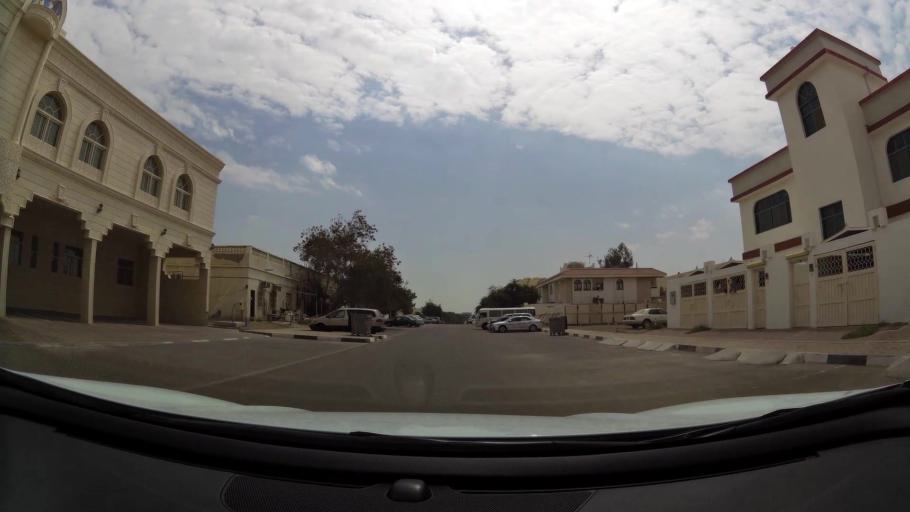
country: AE
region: Abu Dhabi
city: Al Ain
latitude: 24.2132
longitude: 55.7885
